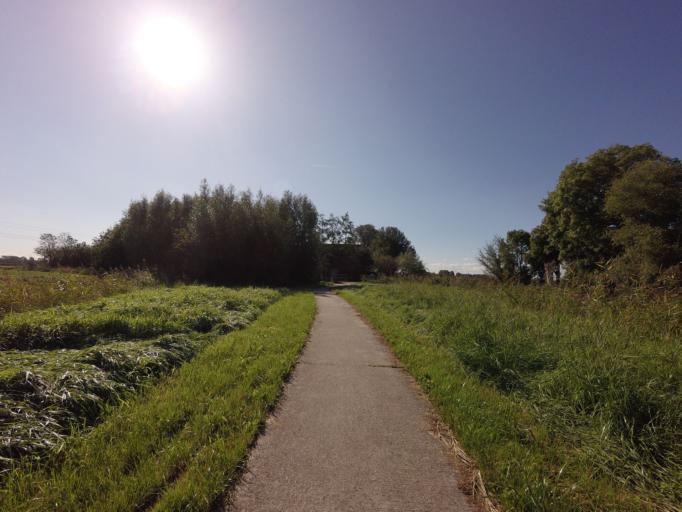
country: NL
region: Friesland
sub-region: Gemeente Leeuwarden
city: Wirdum
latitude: 53.1573
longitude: 5.7656
